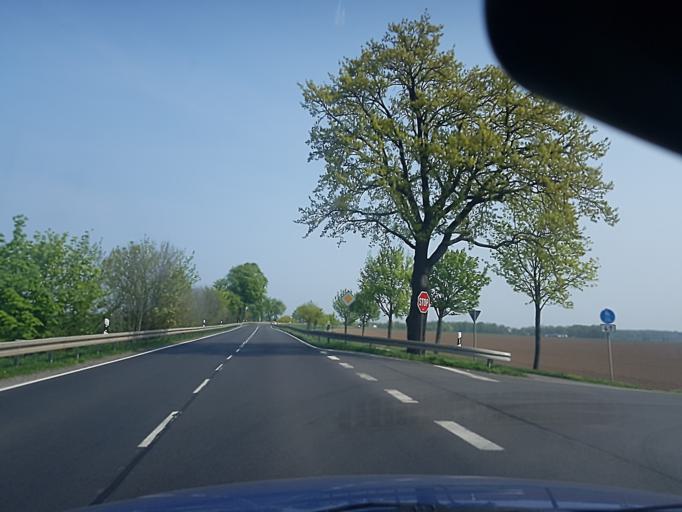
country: DE
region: Saxony
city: Torgau
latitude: 51.5719
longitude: 13.0275
